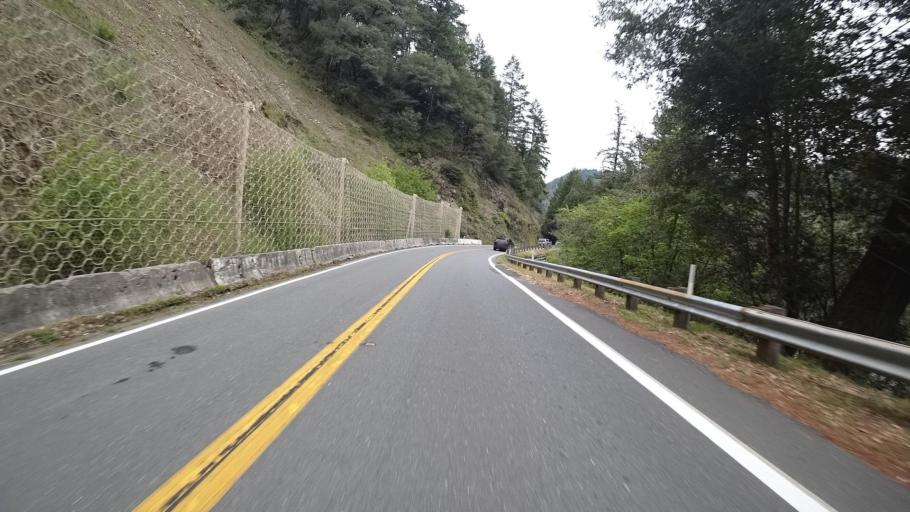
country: US
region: California
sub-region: Humboldt County
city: Willow Creek
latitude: 41.0176
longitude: -123.6370
